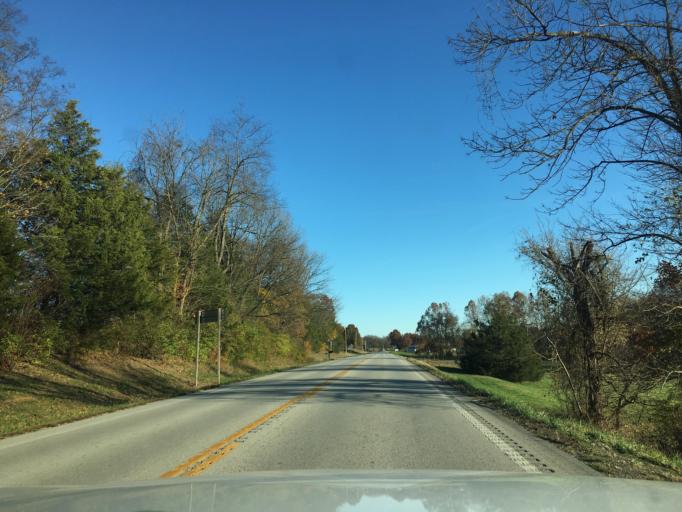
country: US
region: Missouri
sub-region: Franklin County
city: New Haven
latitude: 38.6028
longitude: -91.2611
